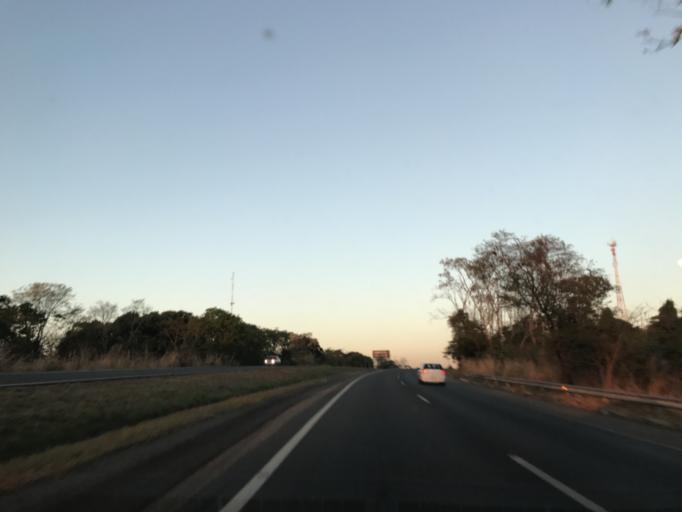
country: BR
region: Goias
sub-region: Abadiania
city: Abadiania
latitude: -16.1602
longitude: -48.6144
